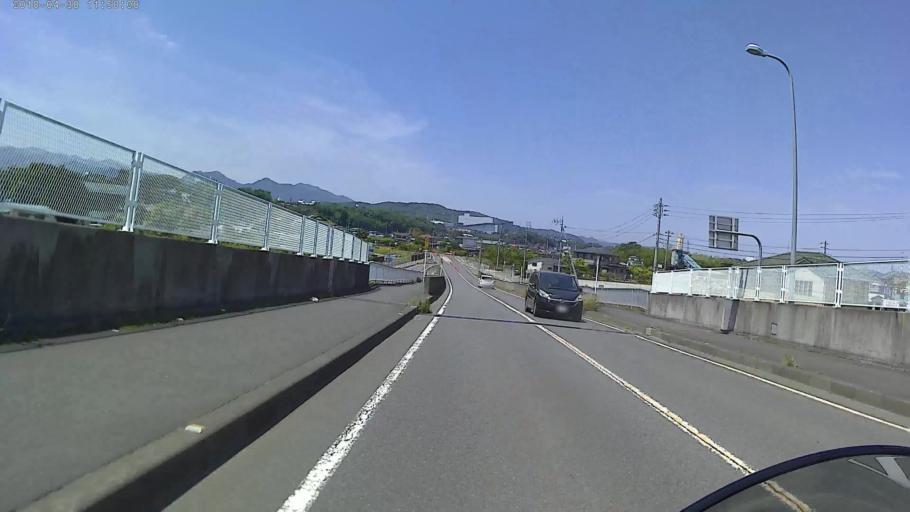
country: JP
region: Kanagawa
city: Zama
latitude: 35.4833
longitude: 139.3532
